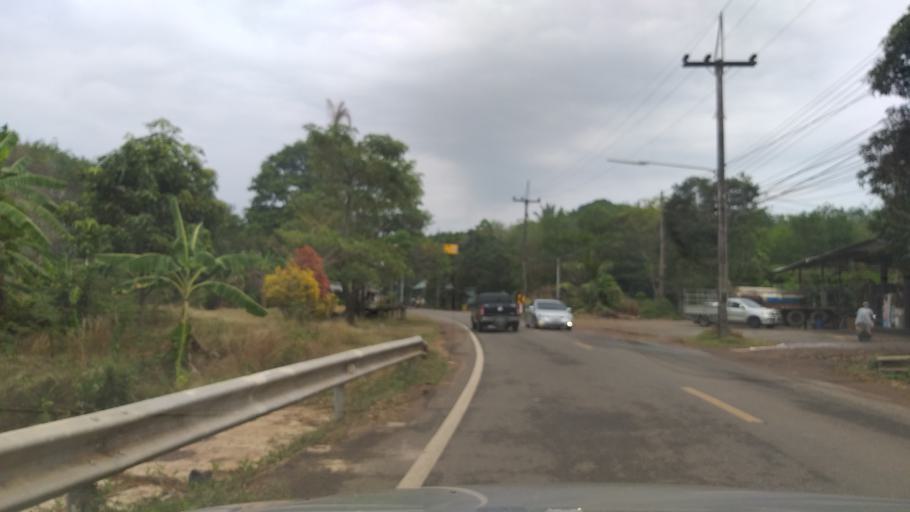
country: TH
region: Trat
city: Laem Ngop
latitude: 12.2147
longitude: 102.3043
